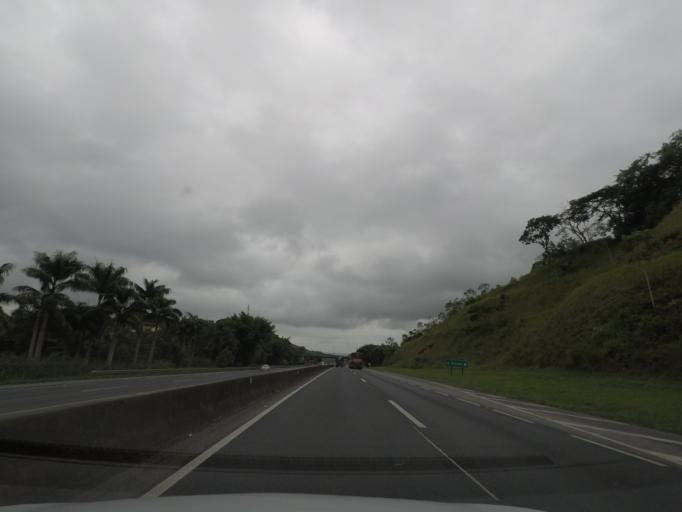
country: BR
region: Sao Paulo
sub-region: Registro
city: Registro
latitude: -24.4044
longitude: -47.7414
